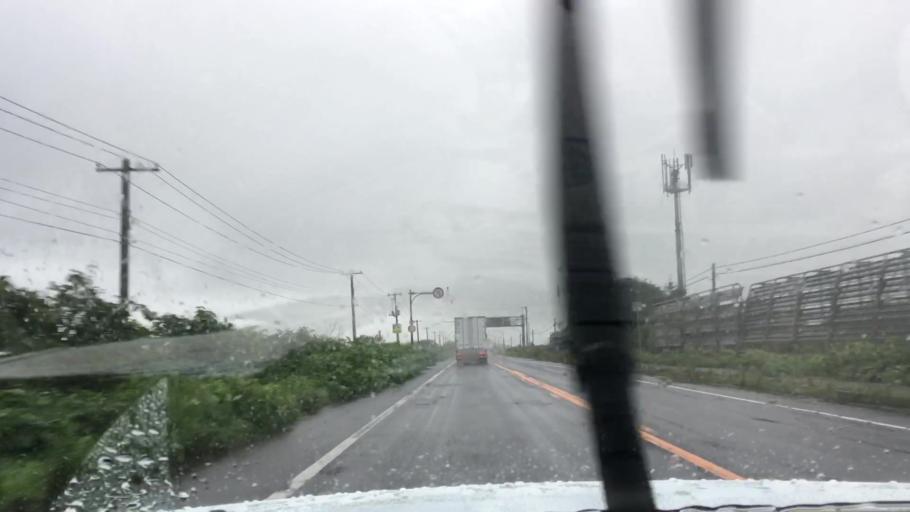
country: JP
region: Hokkaido
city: Niseko Town
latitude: 42.4316
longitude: 140.3186
